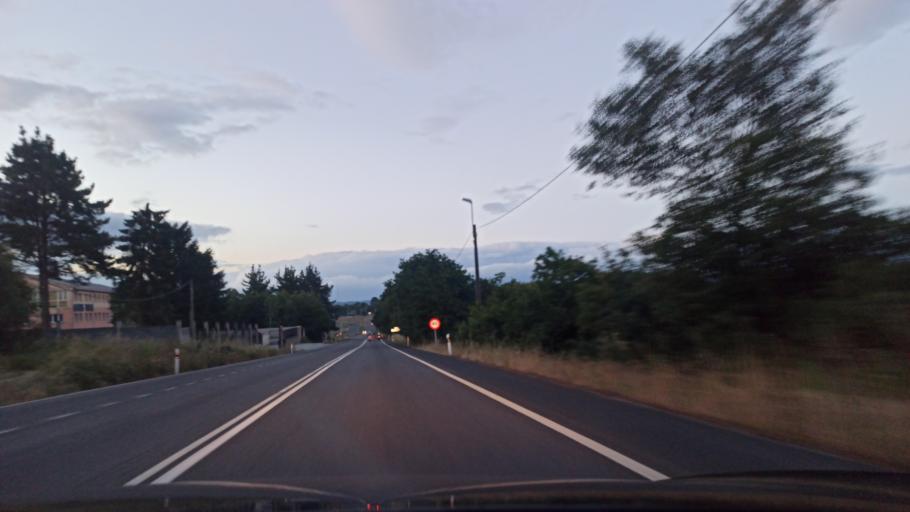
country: ES
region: Galicia
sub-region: Provincia de Lugo
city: Lugo
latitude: 42.9740
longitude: -7.5919
